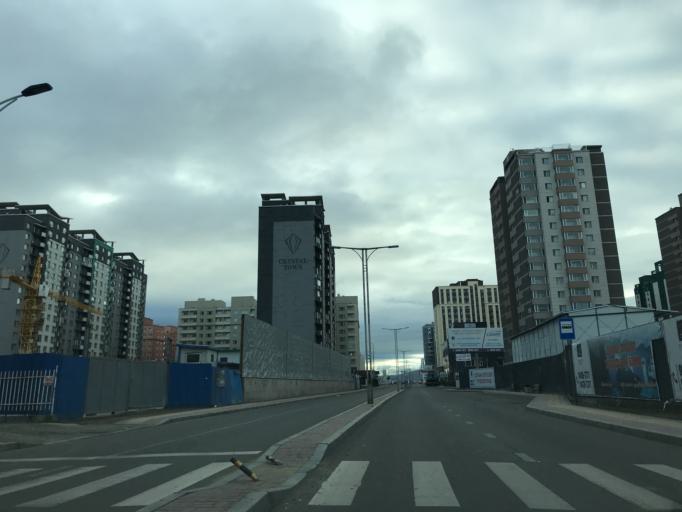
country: MN
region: Ulaanbaatar
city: Ulaanbaatar
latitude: 47.9048
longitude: 106.9387
